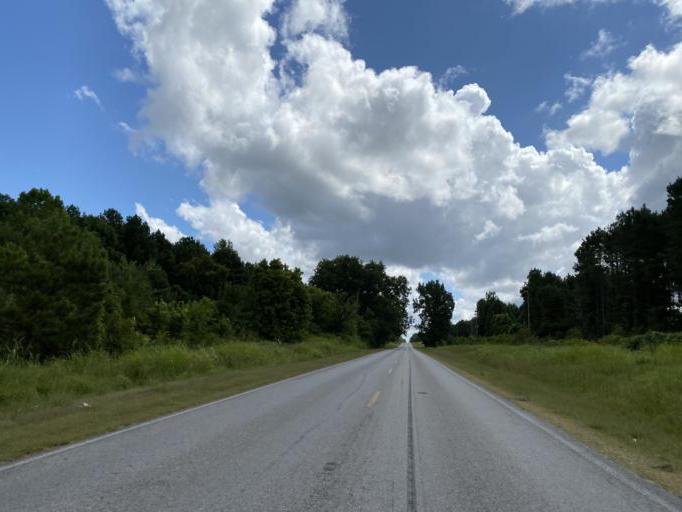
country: US
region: Mississippi
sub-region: Panola County
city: Como
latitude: 34.5105
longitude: -90.0188
